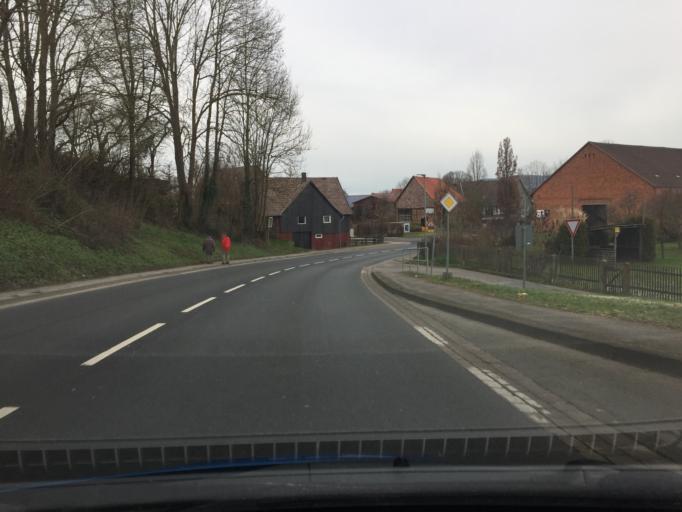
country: DE
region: Lower Saxony
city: Eschershausen
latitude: 51.9363
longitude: 9.6326
